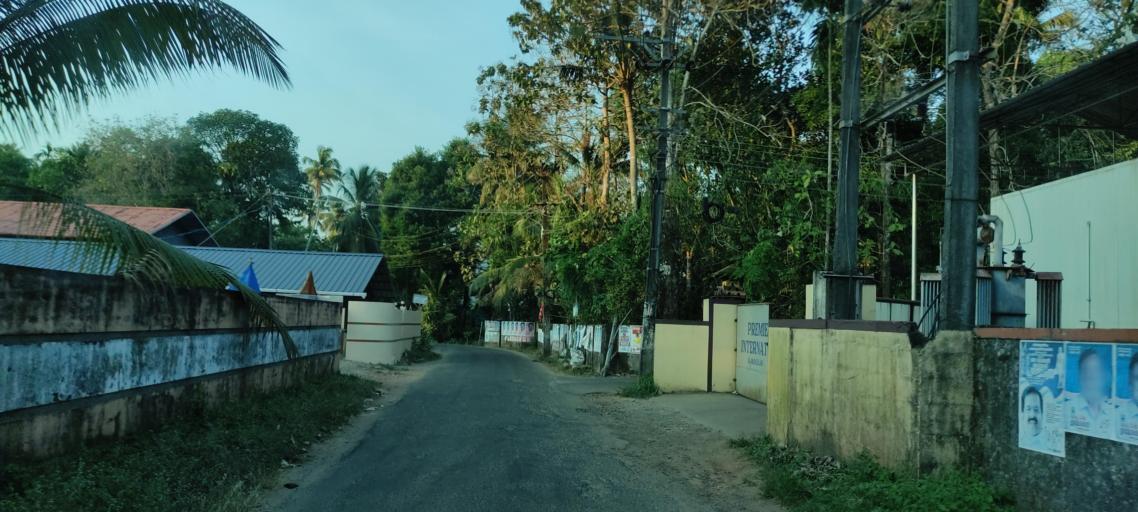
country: IN
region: Kerala
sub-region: Alappuzha
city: Kutiatodu
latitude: 9.7829
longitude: 76.3246
